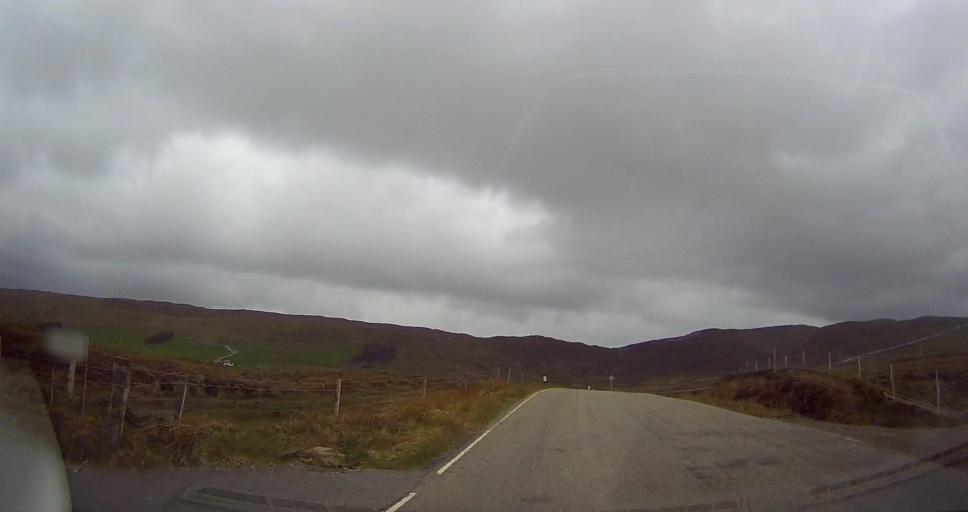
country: GB
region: Scotland
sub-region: Shetland Islands
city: Lerwick
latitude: 60.2771
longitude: -1.2634
